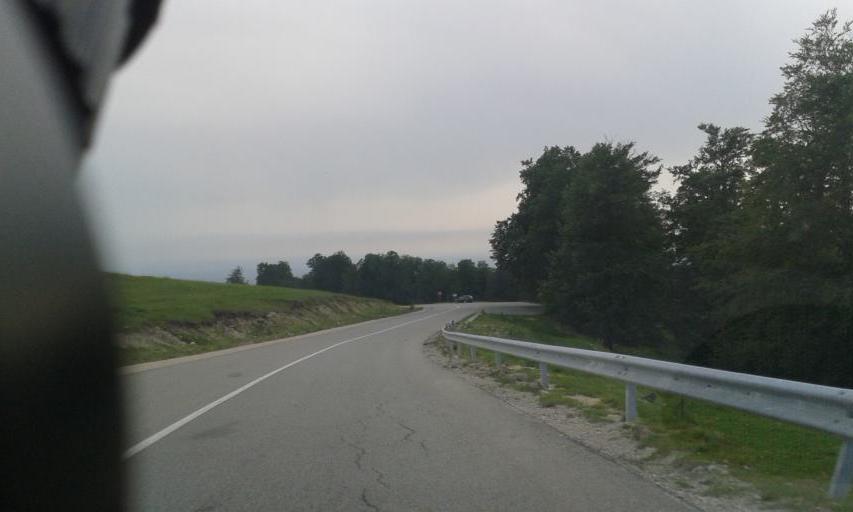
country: RO
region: Gorj
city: Novaci-Straini
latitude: 45.2383
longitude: 23.6935
